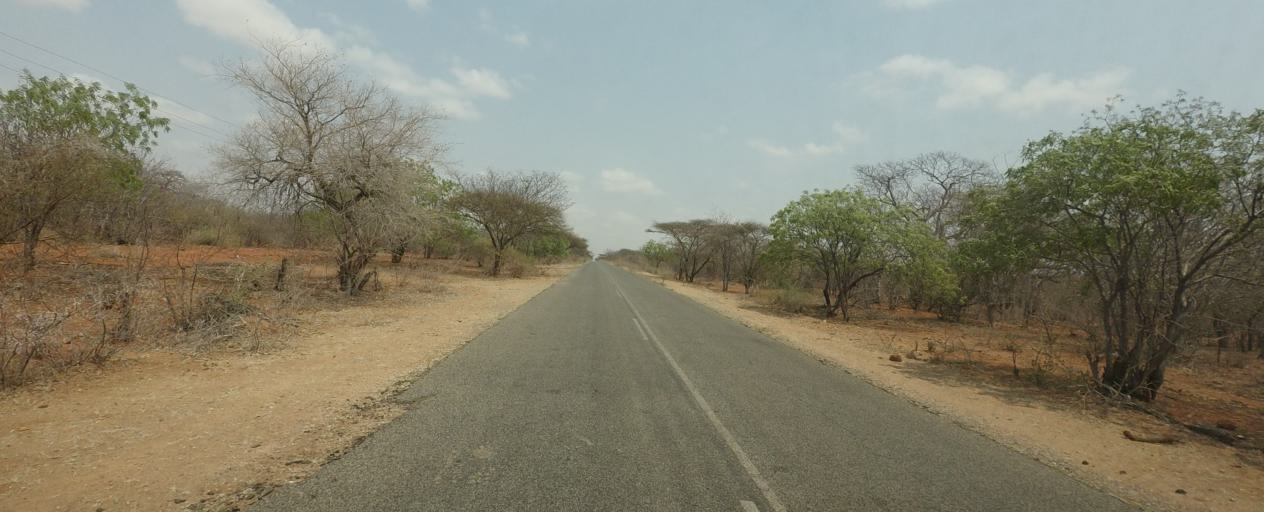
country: ZA
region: Limpopo
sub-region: Vhembe District Municipality
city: Mutale
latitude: -22.4209
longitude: 30.9268
